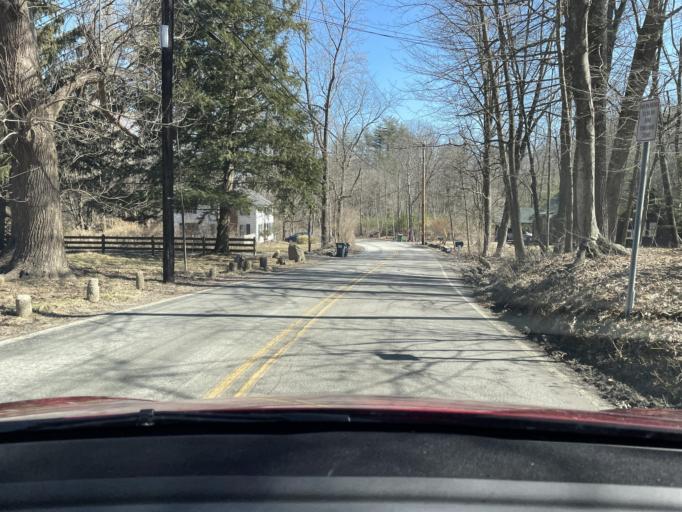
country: US
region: New York
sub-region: Ulster County
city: Woodstock
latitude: 42.0357
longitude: -74.1222
